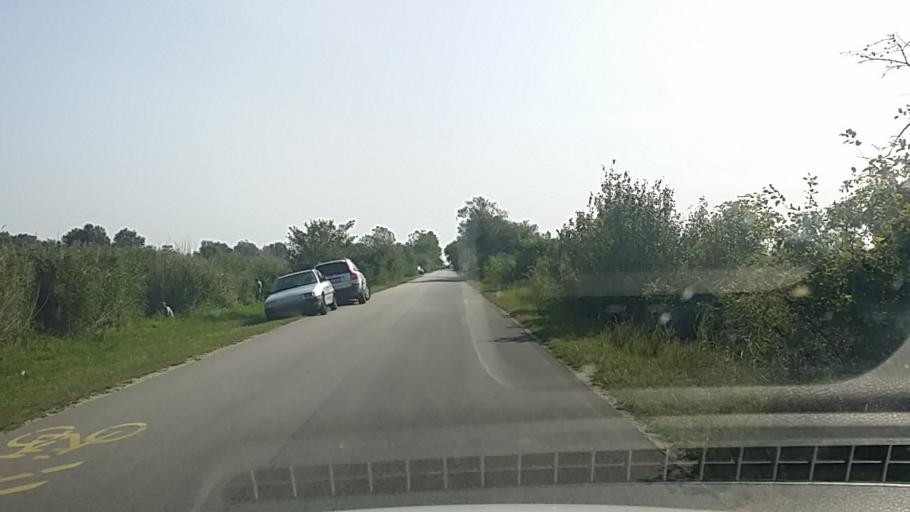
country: HU
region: Gyor-Moson-Sopron
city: Fertorakos
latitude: 47.7197
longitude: 16.6848
